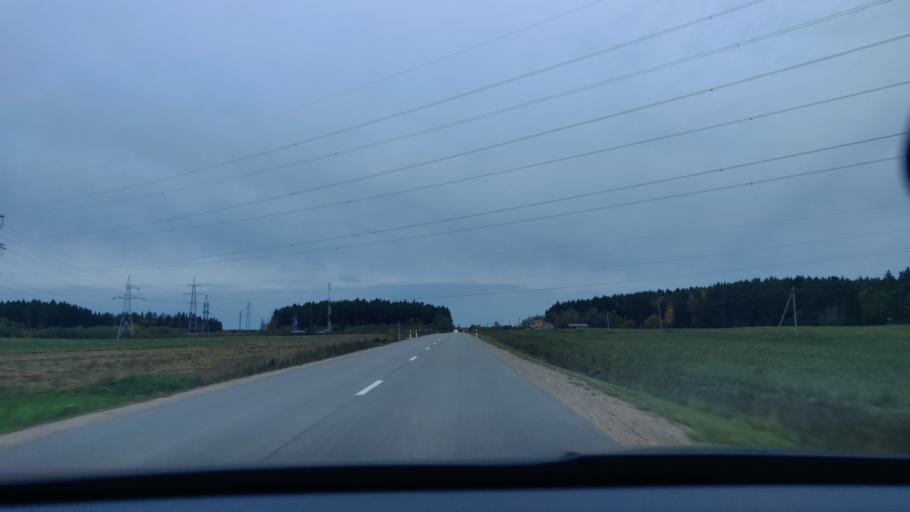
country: LT
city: Lentvaris
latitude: 54.5961
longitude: 25.0342
